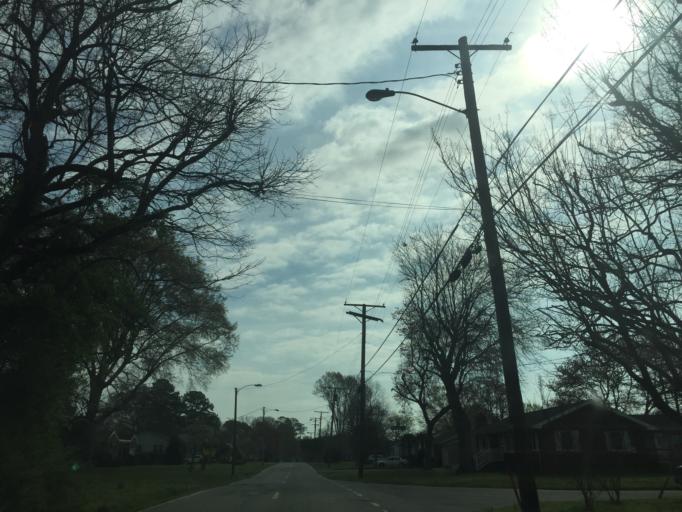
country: US
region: Virginia
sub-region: City of Newport News
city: Newport News
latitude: 37.0712
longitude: -76.4635
